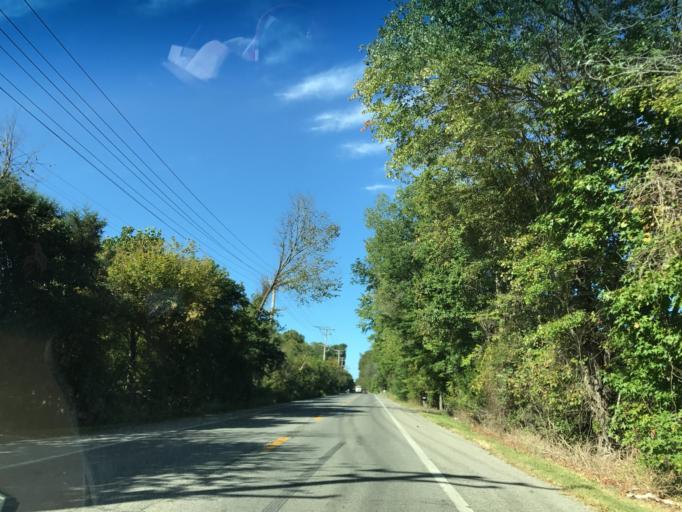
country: US
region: Maryland
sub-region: Prince George's County
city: Bowie
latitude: 38.9036
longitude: -76.6879
